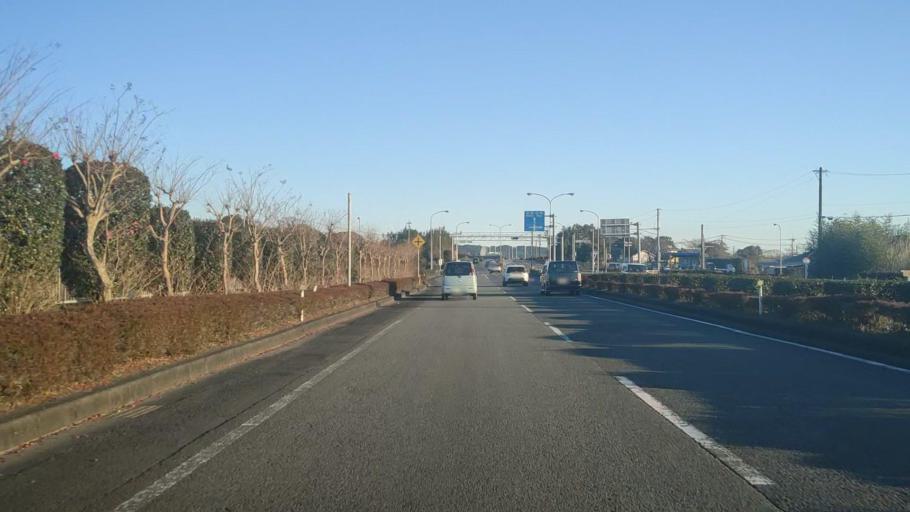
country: JP
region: Miyazaki
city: Tsuma
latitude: 32.0432
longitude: 131.4701
